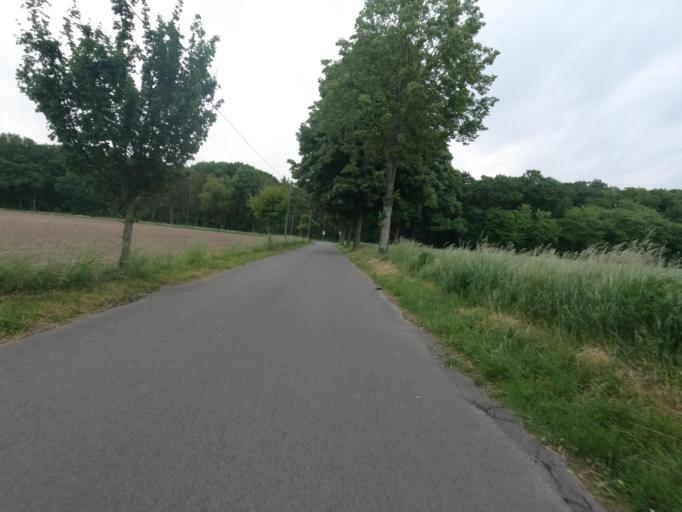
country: NL
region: Limburg
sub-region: Gemeente Roerdalen
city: Vlodrop
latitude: 51.1302
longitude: 6.1068
